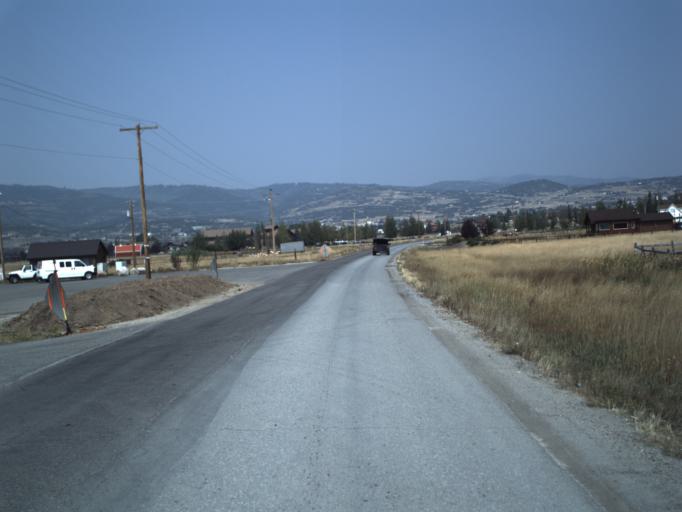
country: US
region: Utah
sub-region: Summit County
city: Snyderville
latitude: 40.7362
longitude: -111.4999
